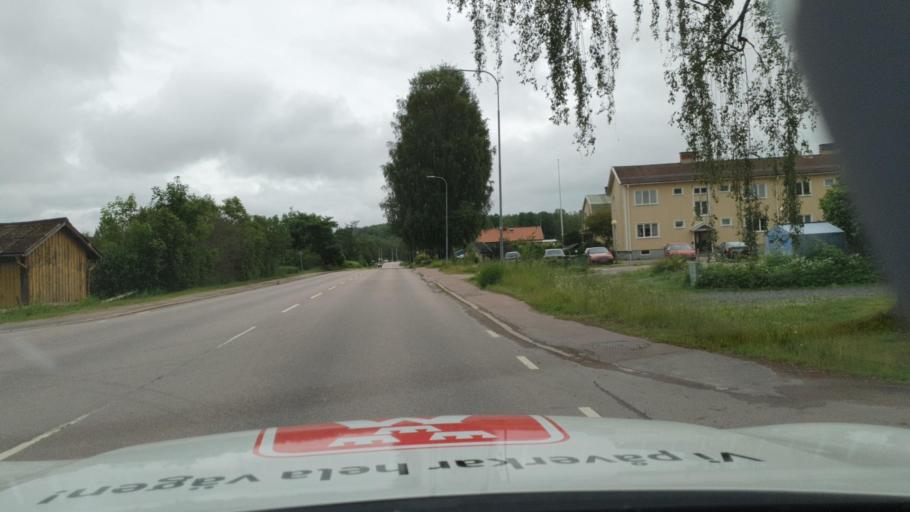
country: SE
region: Vaermland
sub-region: Karlstads Kommun
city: Valberg
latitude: 59.3987
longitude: 13.1990
